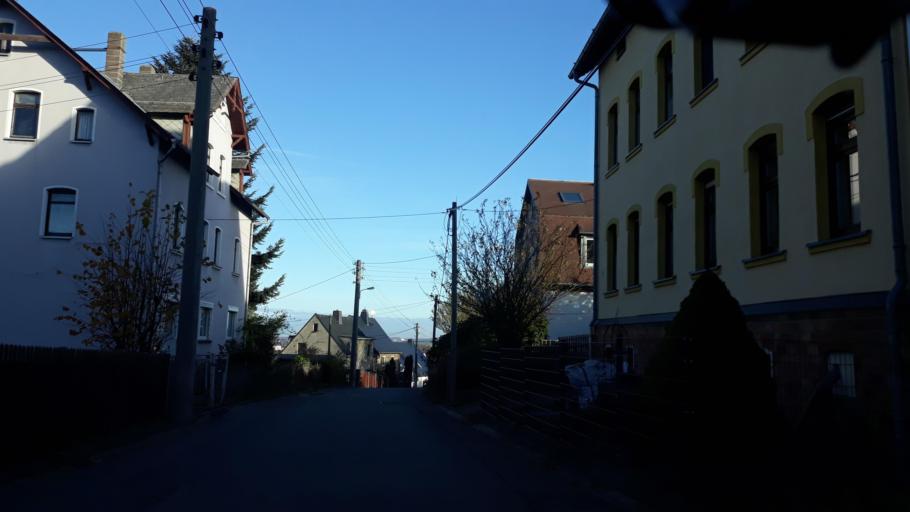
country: DE
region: Saxony
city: Wilkau-Hasslau
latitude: 50.6570
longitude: 12.5095
